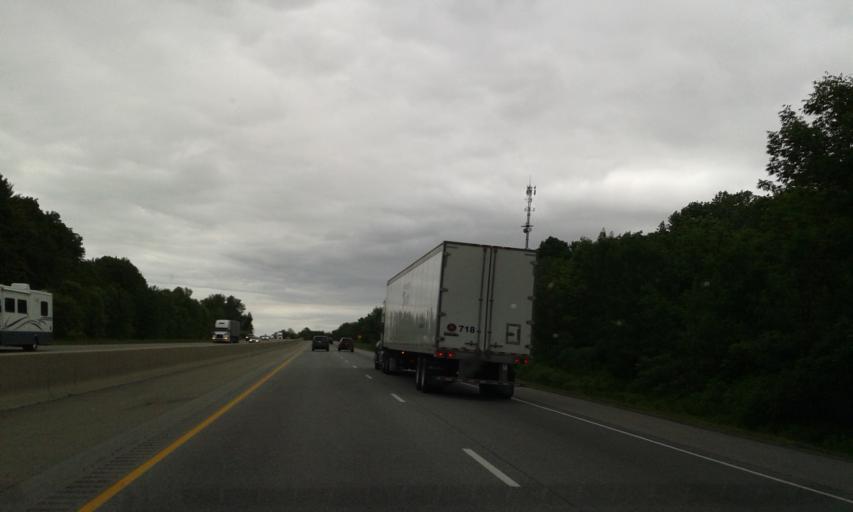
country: CA
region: Ontario
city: Brockville
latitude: 44.5906
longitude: -75.7155
